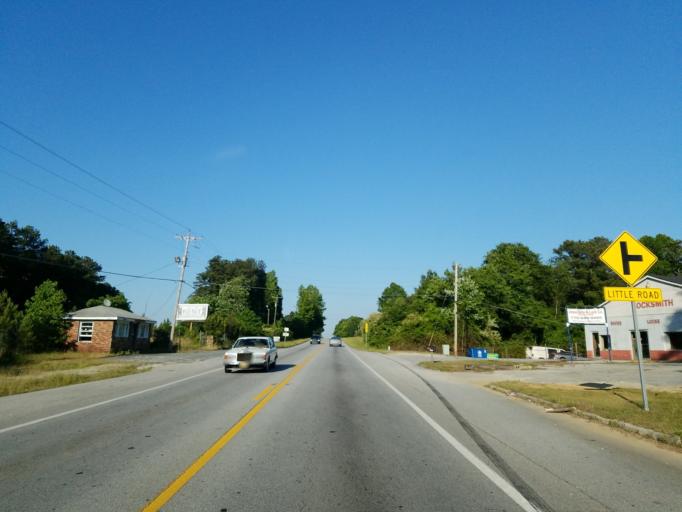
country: US
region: Georgia
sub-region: Douglas County
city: Lithia Springs
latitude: 33.7911
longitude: -84.6917
